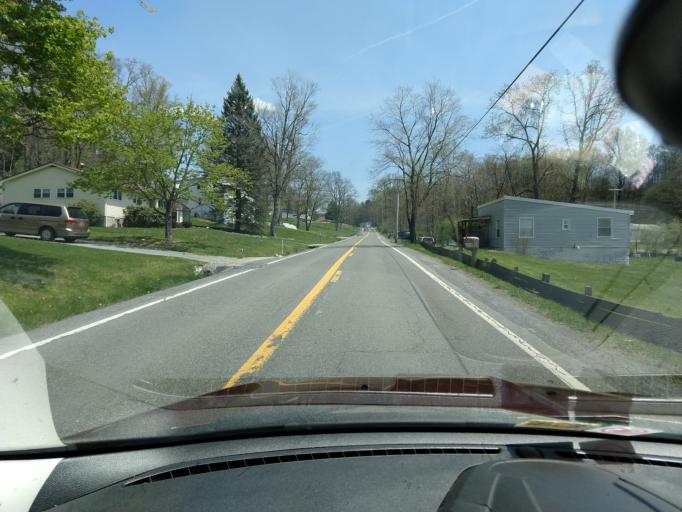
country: US
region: West Virginia
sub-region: Raleigh County
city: Bradley
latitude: 37.8530
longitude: -81.2039
